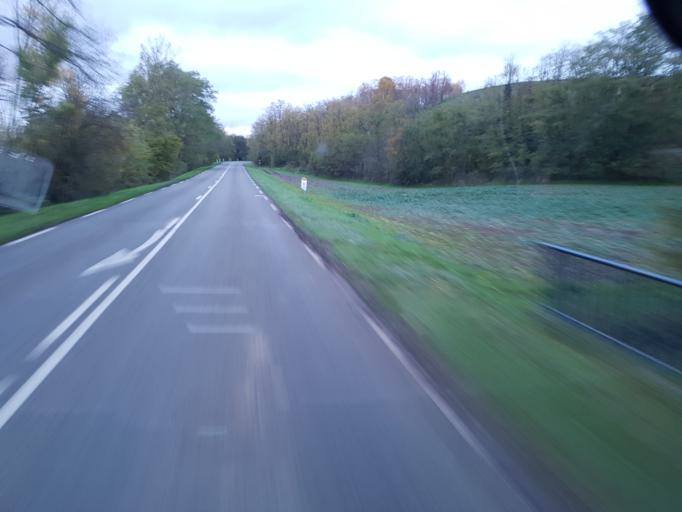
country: FR
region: Picardie
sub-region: Departement de l'Aisne
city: Coincy
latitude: 49.1407
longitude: 3.3877
